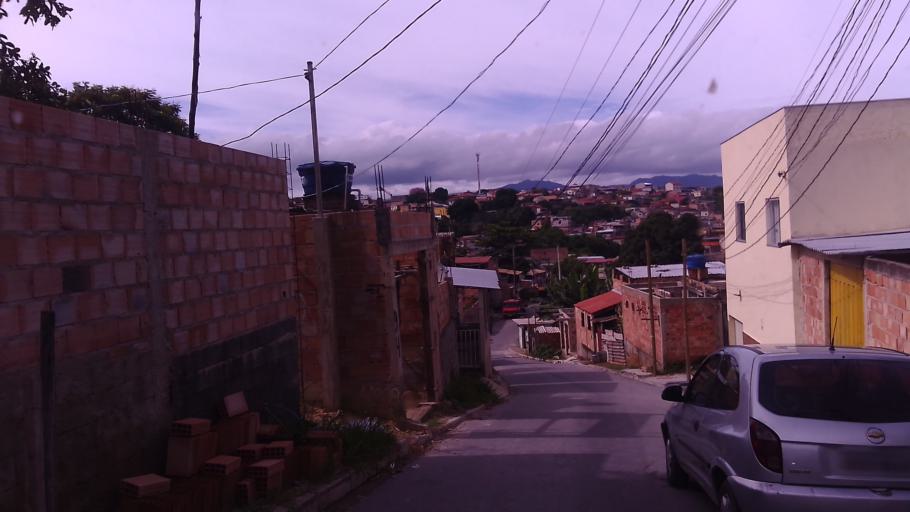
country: BR
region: Minas Gerais
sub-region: Santa Luzia
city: Santa Luzia
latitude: -19.8395
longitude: -43.8981
